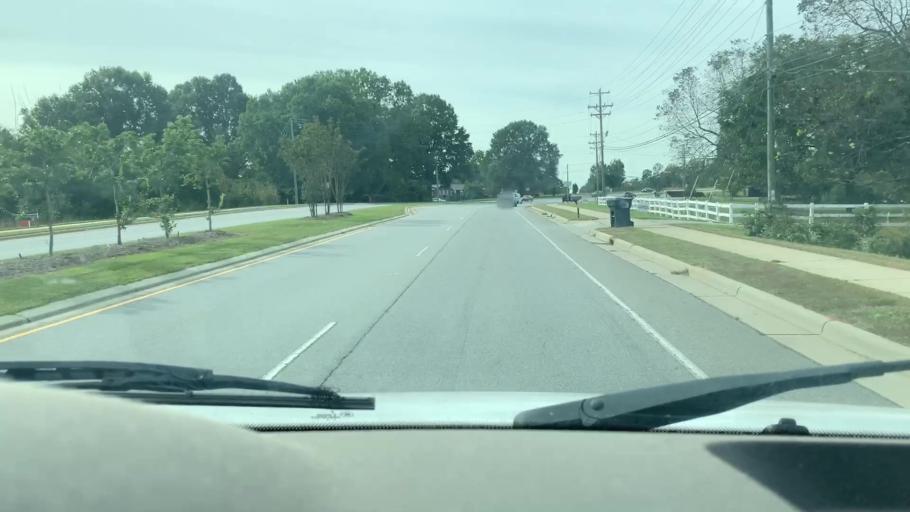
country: US
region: North Carolina
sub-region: Catawba County
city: Lake Norman of Catawba
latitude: 35.5706
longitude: -80.8972
